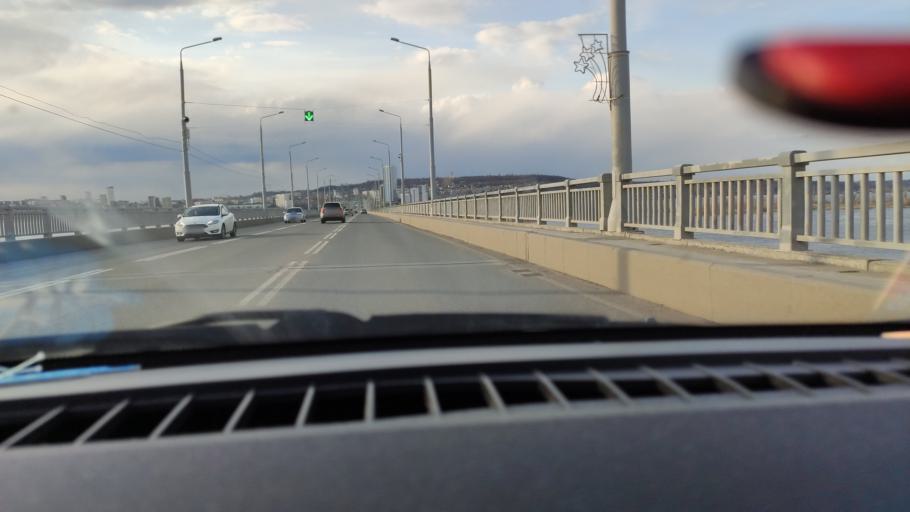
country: RU
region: Saratov
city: Engel's
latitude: 51.5134
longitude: 46.0731
